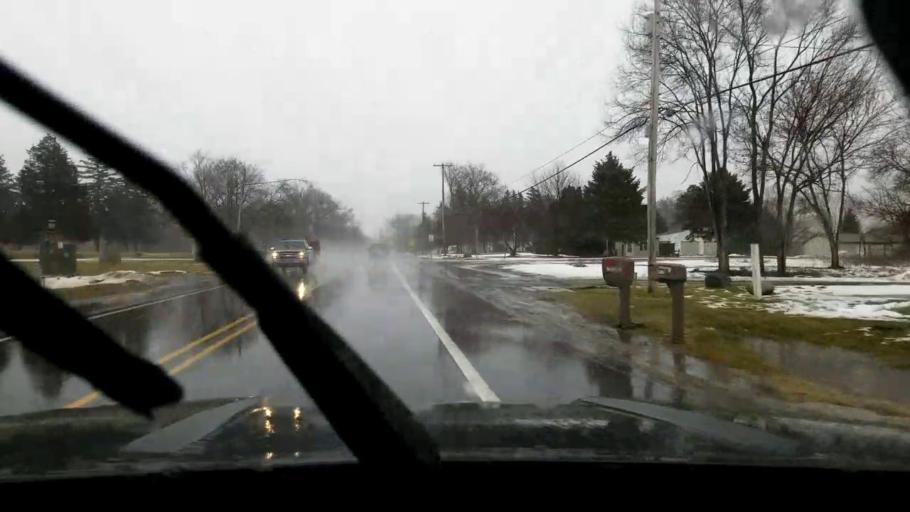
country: US
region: Michigan
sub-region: Jackson County
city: Vandercook Lake
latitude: 42.1969
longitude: -84.3491
